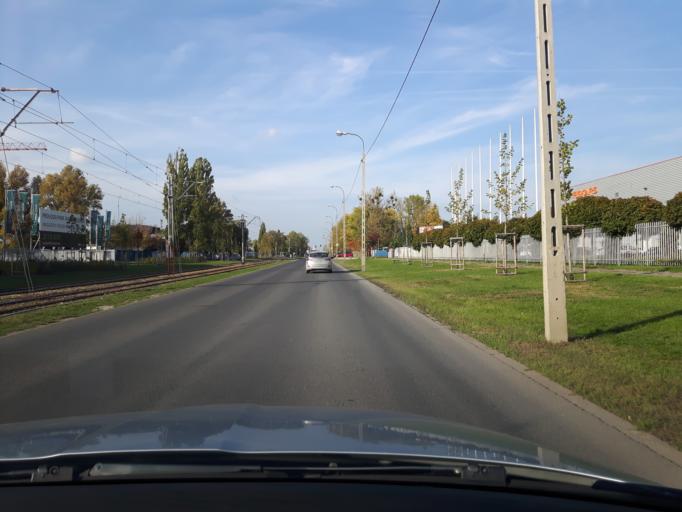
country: PL
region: Masovian Voivodeship
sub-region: Warszawa
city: Targowek
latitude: 52.3031
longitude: 21.0201
